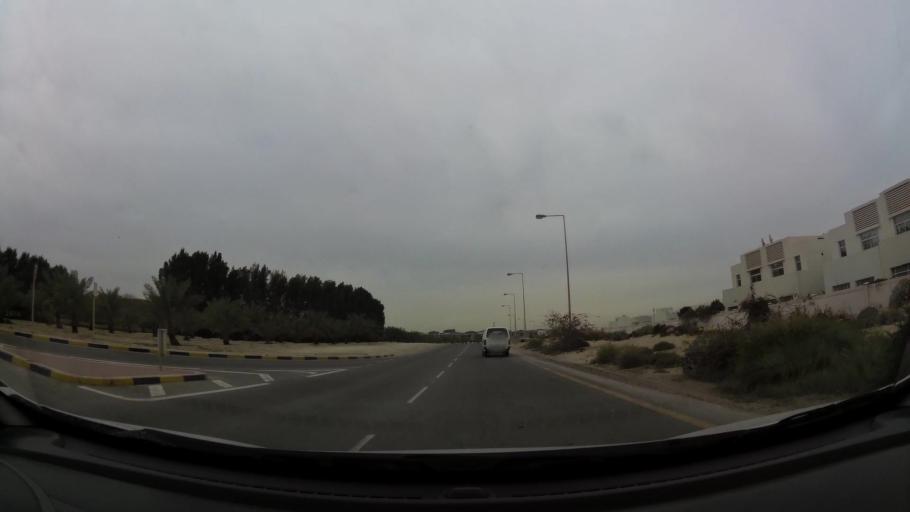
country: BH
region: Northern
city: Ar Rifa'
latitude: 26.0916
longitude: 50.5634
